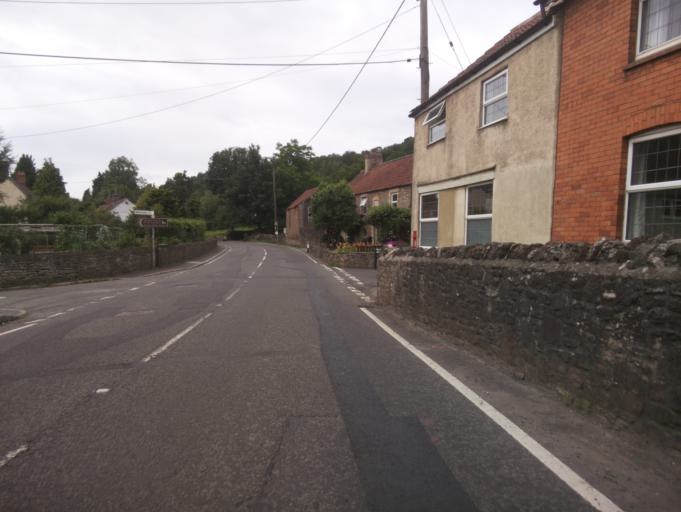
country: GB
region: England
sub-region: Somerset
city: Bradley Cross
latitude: 51.2479
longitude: -2.7368
